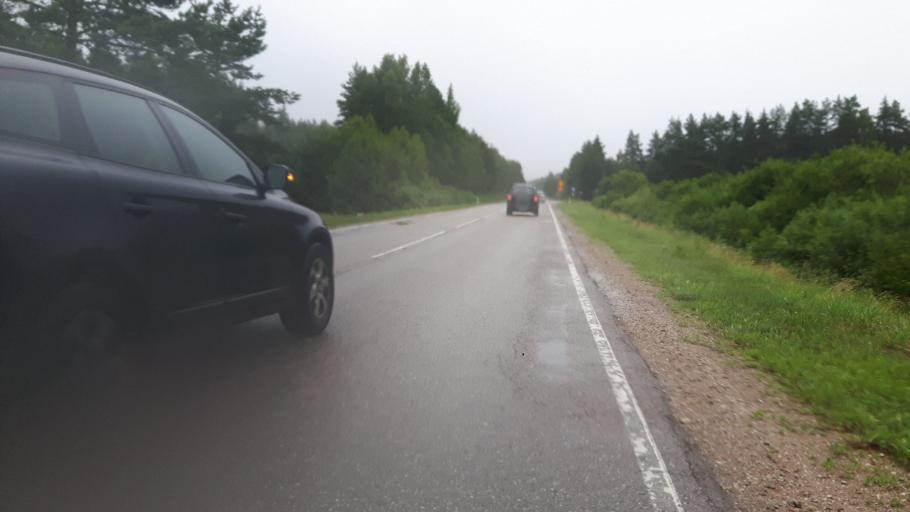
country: LV
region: Rucavas
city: Rucava
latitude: 56.1043
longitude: 21.1360
